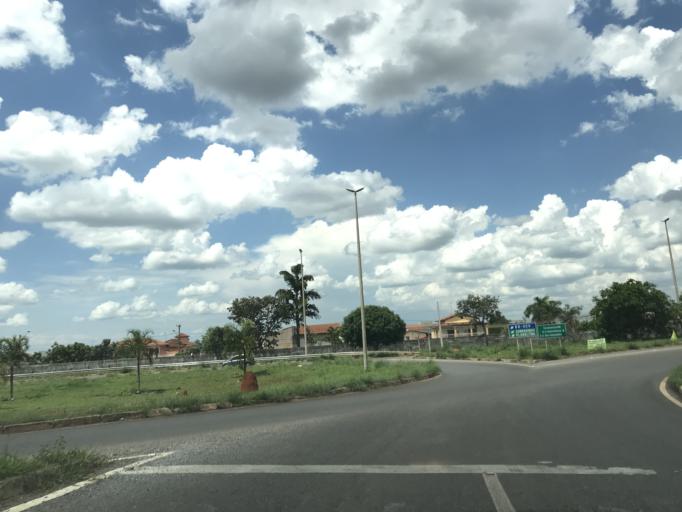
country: BR
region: Federal District
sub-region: Brasilia
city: Brasilia
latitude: -15.6898
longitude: -47.8342
